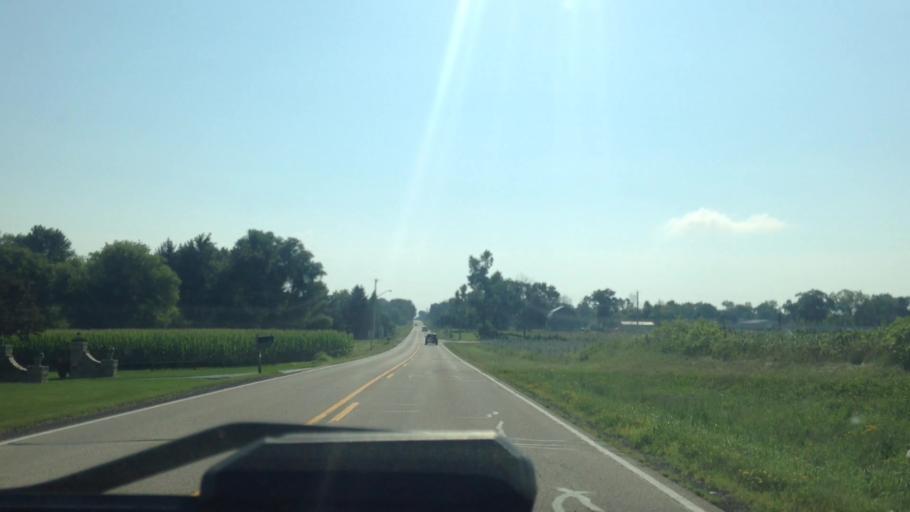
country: US
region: Wisconsin
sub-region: Waukesha County
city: Sussex
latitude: 43.1628
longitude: -88.2253
